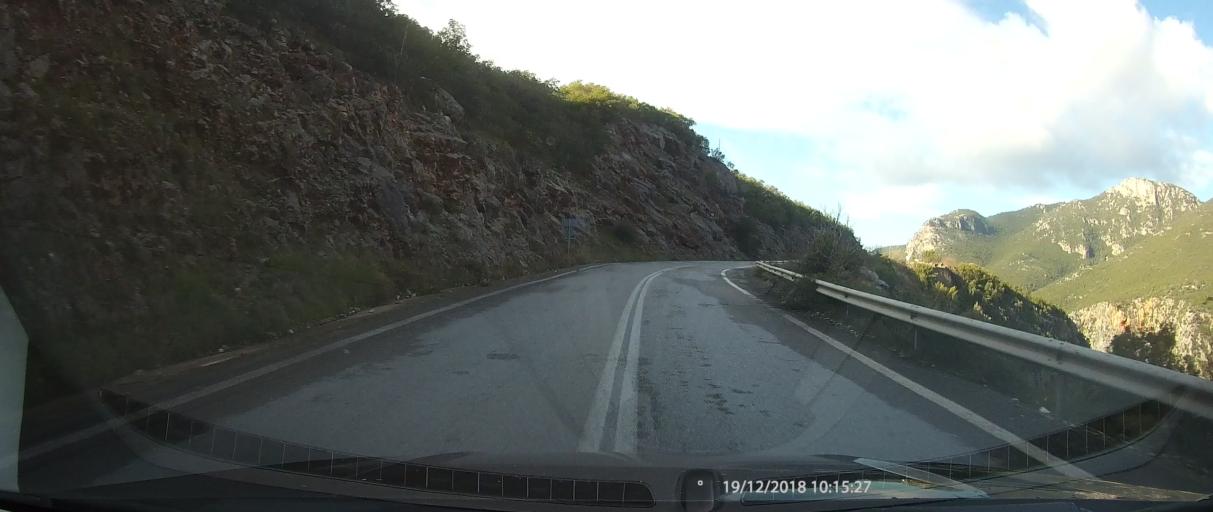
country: GR
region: Peloponnese
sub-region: Nomos Messinias
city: Kalamata
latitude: 37.0820
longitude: 22.1594
